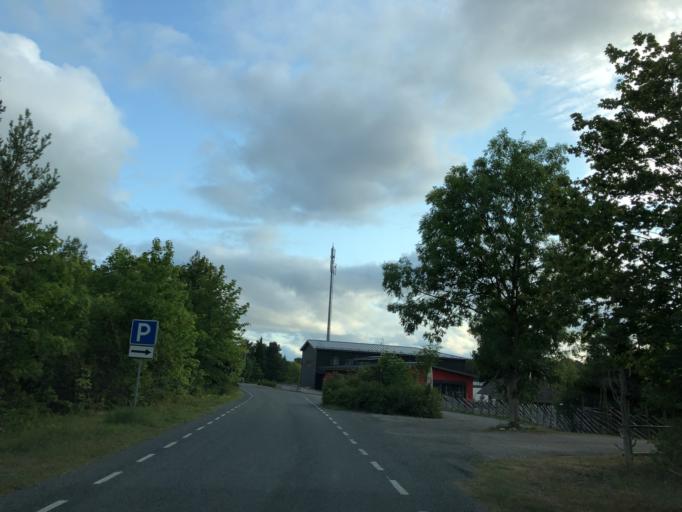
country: EE
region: Hiiumaa
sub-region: Kaerdla linn
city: Kardla
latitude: 58.7885
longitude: 22.8319
